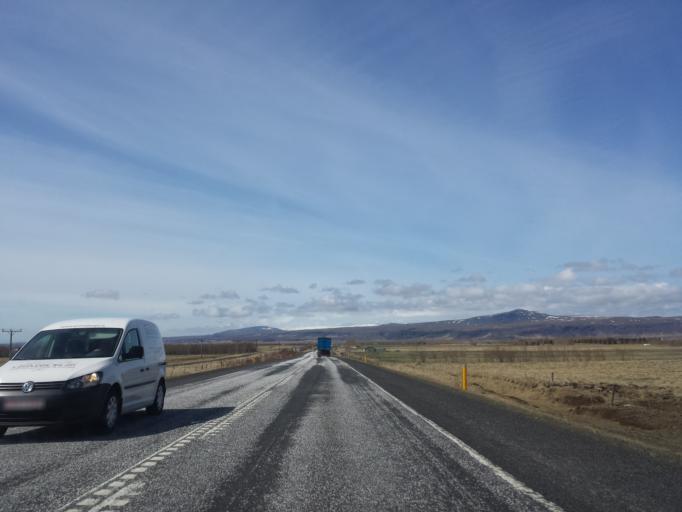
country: IS
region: South
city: Selfoss
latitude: 63.9581
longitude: -21.0828
